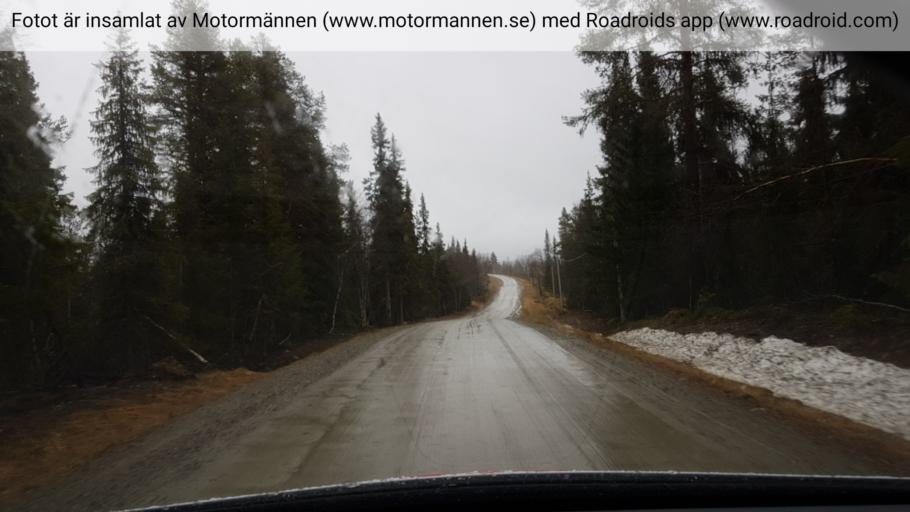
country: SE
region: Jaemtland
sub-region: Are Kommun
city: Jarpen
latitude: 62.6121
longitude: 13.2010
